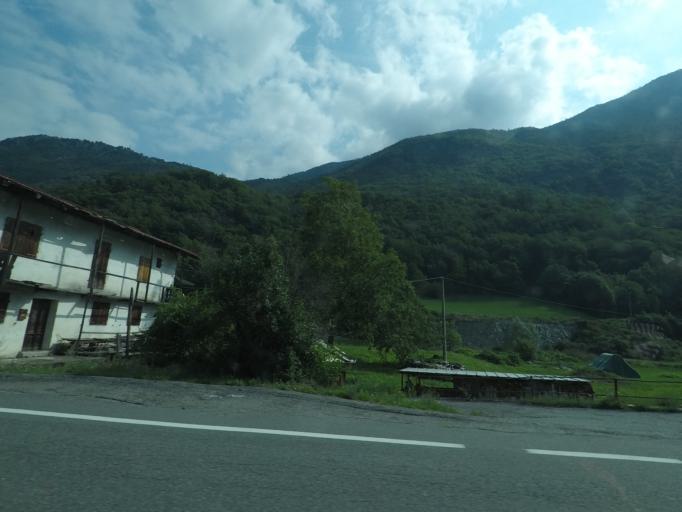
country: IT
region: Aosta Valley
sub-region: Valle d'Aosta
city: Chatillon
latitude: 45.7679
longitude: 7.6016
